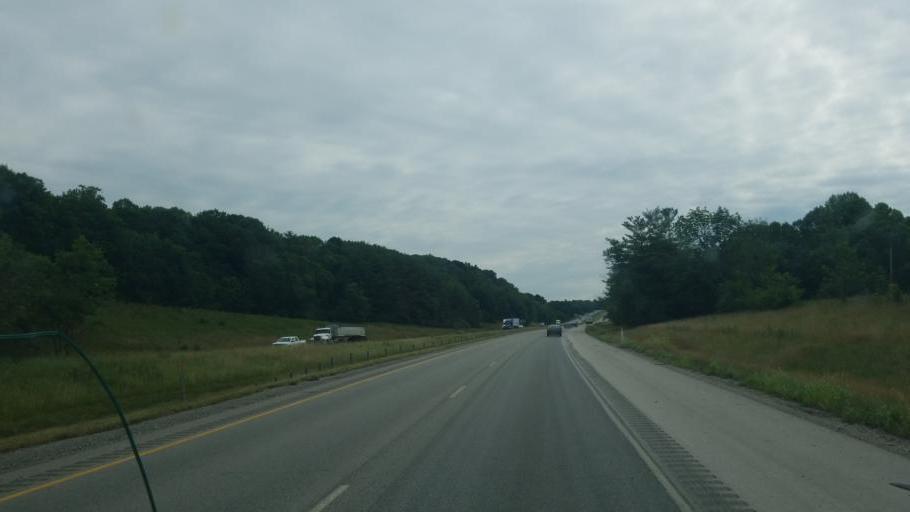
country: US
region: Indiana
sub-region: Putnam County
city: Cloverdale
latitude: 39.5287
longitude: -86.8696
